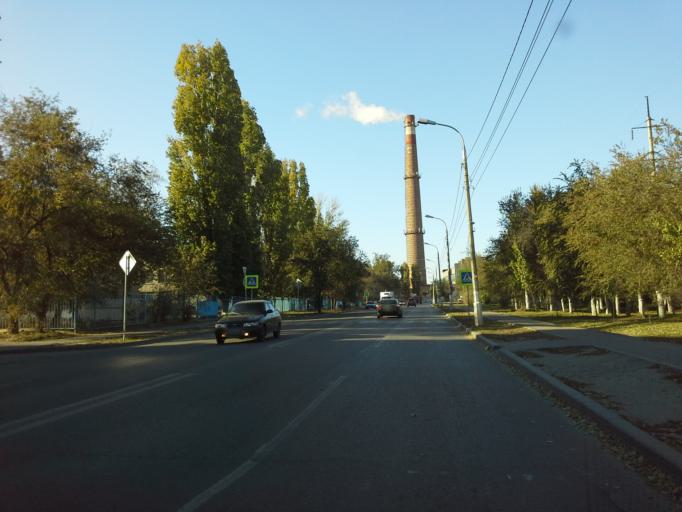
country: RU
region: Volgograd
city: Vodstroy
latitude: 48.8232
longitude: 44.6298
